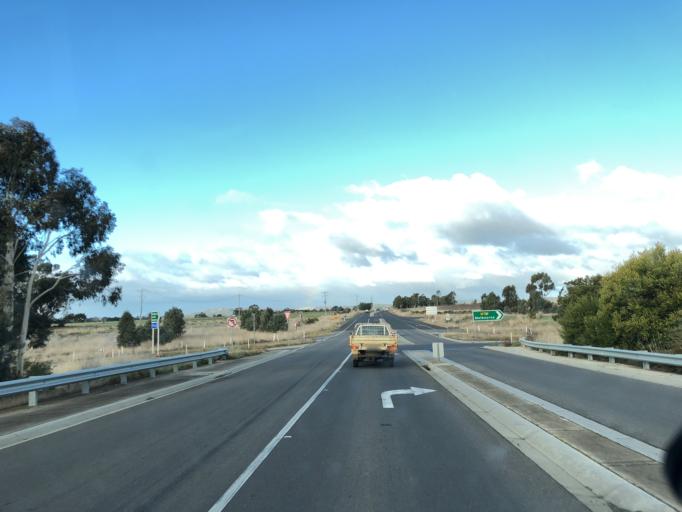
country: AU
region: Victoria
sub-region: Mount Alexander
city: Castlemaine
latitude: -37.1921
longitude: 144.4061
